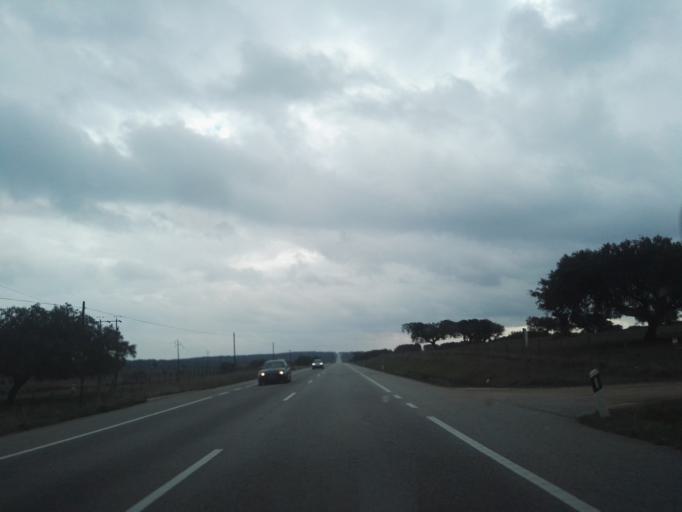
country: PT
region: Portalegre
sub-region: Arronches
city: Arronches
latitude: 39.1684
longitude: -7.3301
